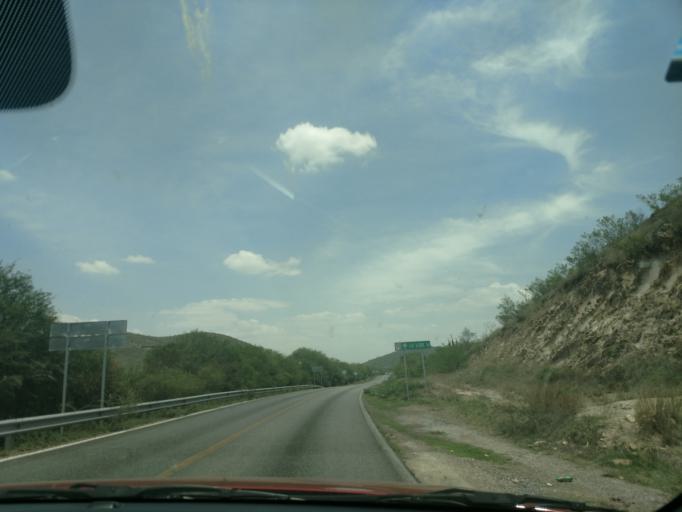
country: MX
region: San Luis Potosi
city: Ciudad Fernandez
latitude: 22.0046
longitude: -100.1465
